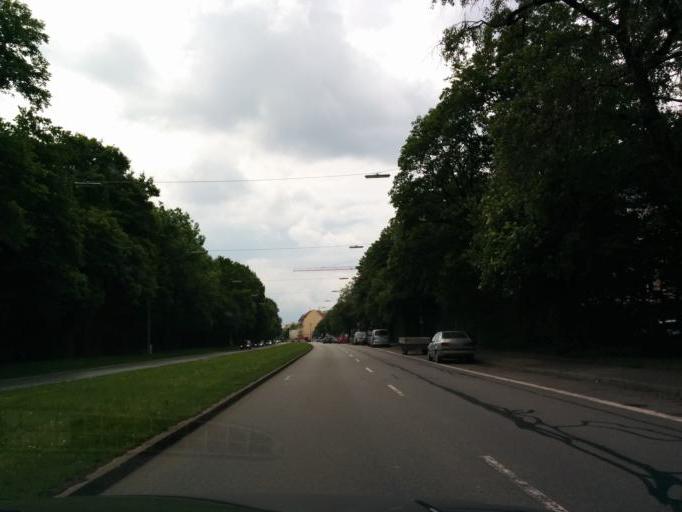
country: DE
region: Bavaria
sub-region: Upper Bavaria
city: Munich
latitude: 48.1070
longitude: 11.5400
